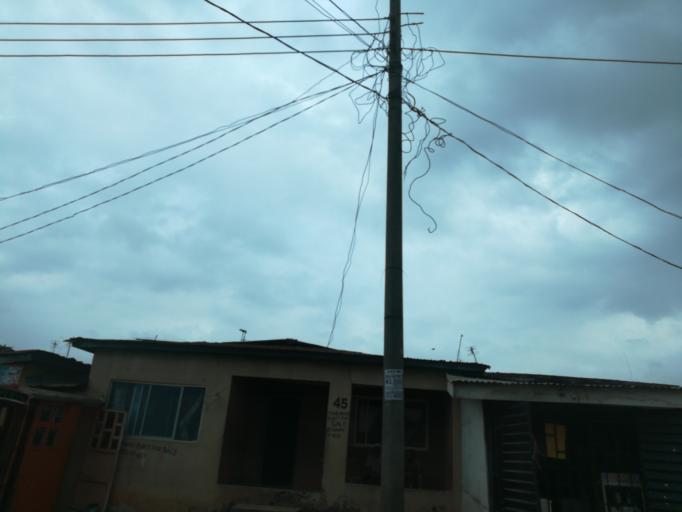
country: NG
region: Lagos
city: Oshodi
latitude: 6.5528
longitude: 3.3338
